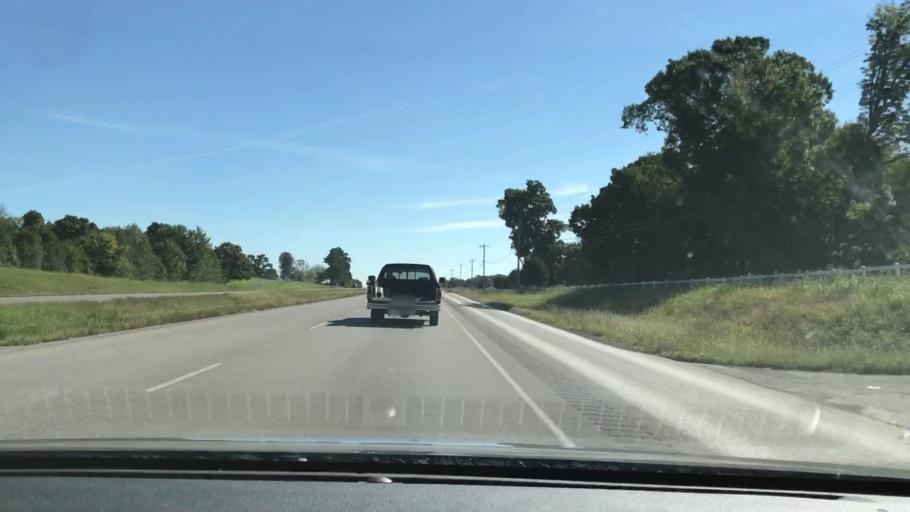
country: US
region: Kentucky
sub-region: Christian County
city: Hopkinsville
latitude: 36.8510
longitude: -87.3659
